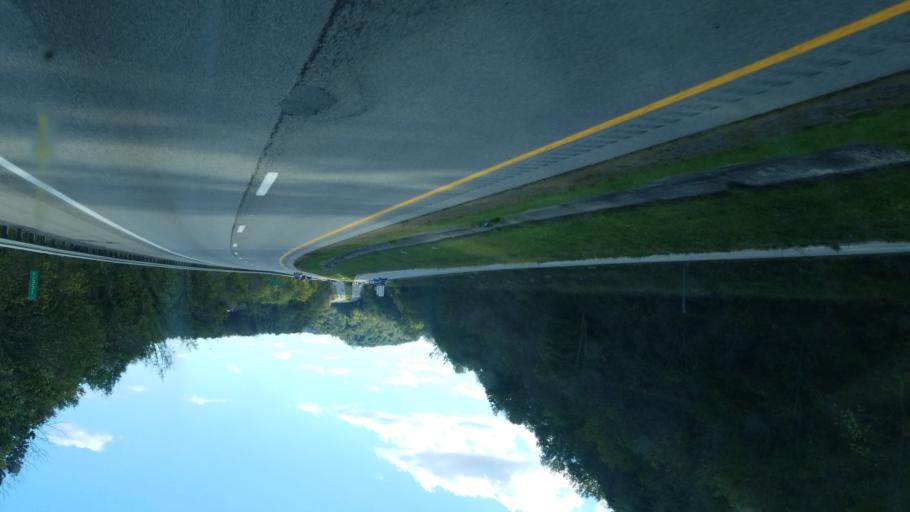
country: US
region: West Virginia
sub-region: Monongalia County
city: Star City
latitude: 39.6638
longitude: -80.0131
